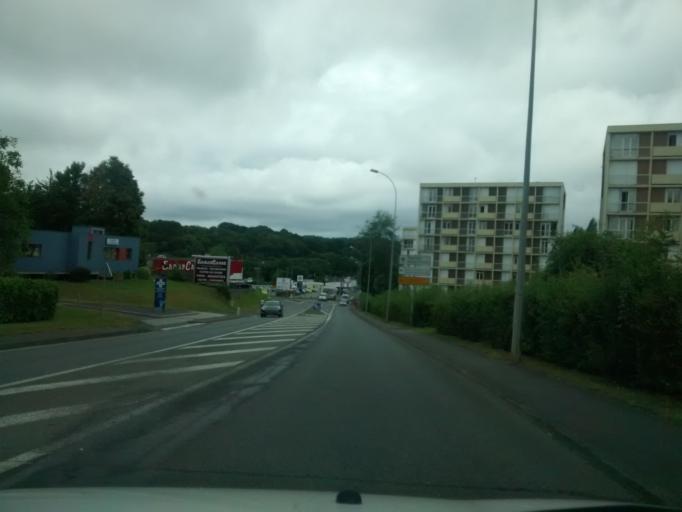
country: FR
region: Brittany
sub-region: Departement des Cotes-d'Armor
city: Lannion
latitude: 48.7265
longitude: -3.4463
